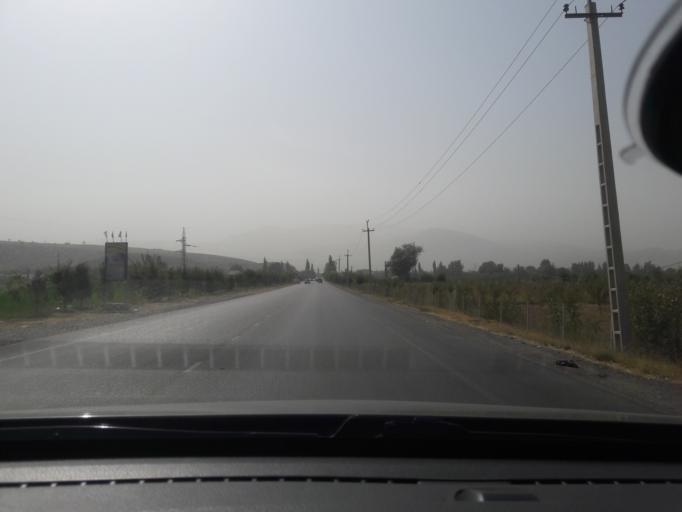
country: TJ
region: Republican Subordination
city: Vahdat
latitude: 38.5289
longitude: 69.0264
